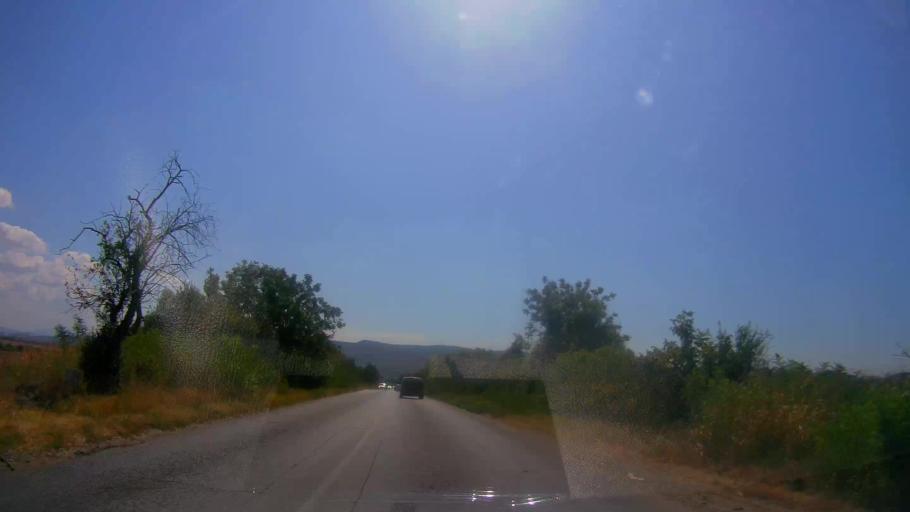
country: BG
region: Veliko Turnovo
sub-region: Obshtina Gorna Oryakhovitsa
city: Purvomaytsi
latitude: 43.1654
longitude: 25.6174
